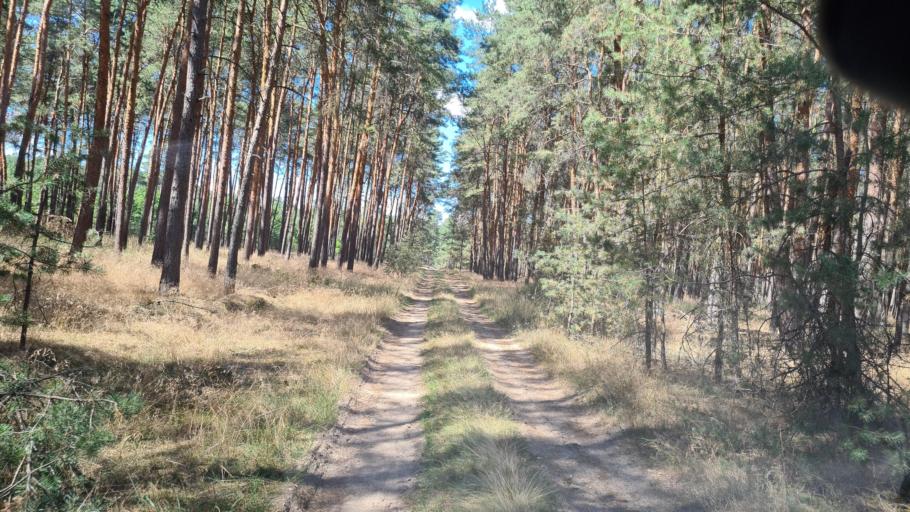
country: DE
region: Brandenburg
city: Treuenbrietzen
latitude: 52.0505
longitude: 12.8119
